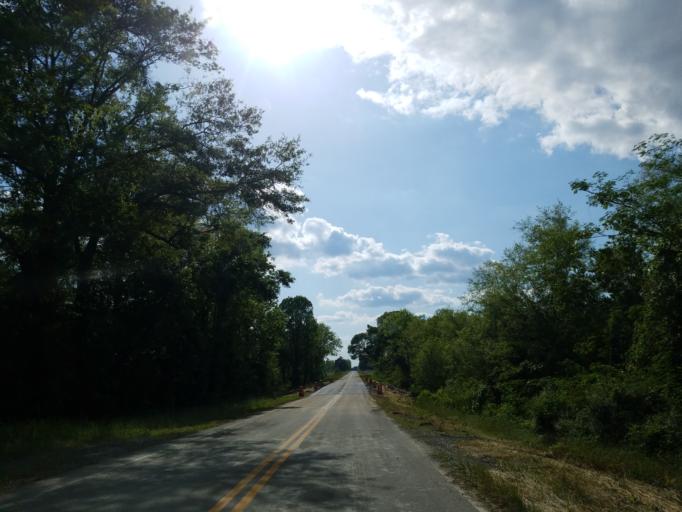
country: US
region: Georgia
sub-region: Dooly County
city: Vienna
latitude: 32.1527
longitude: -83.7763
